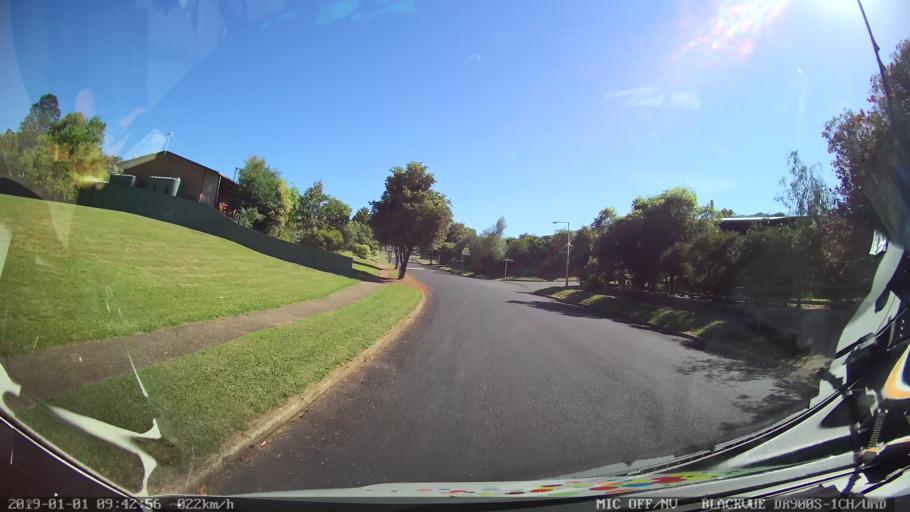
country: AU
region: New South Wales
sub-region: Snowy River
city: Jindabyne
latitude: -36.2158
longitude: 148.1321
